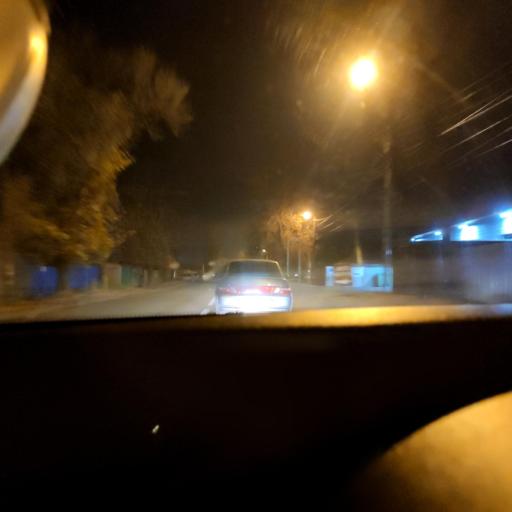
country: RU
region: Samara
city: Smyshlyayevka
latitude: 53.2399
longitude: 50.3263
